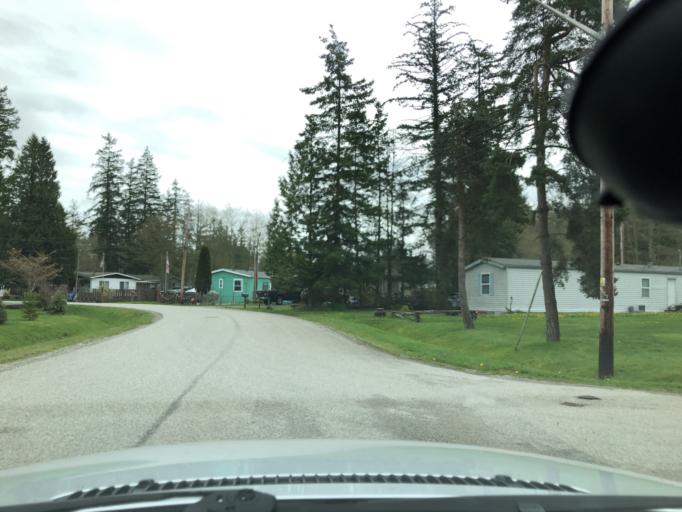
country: US
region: Washington
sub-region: Whatcom County
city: Birch Bay
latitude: 48.9544
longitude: -122.7318
